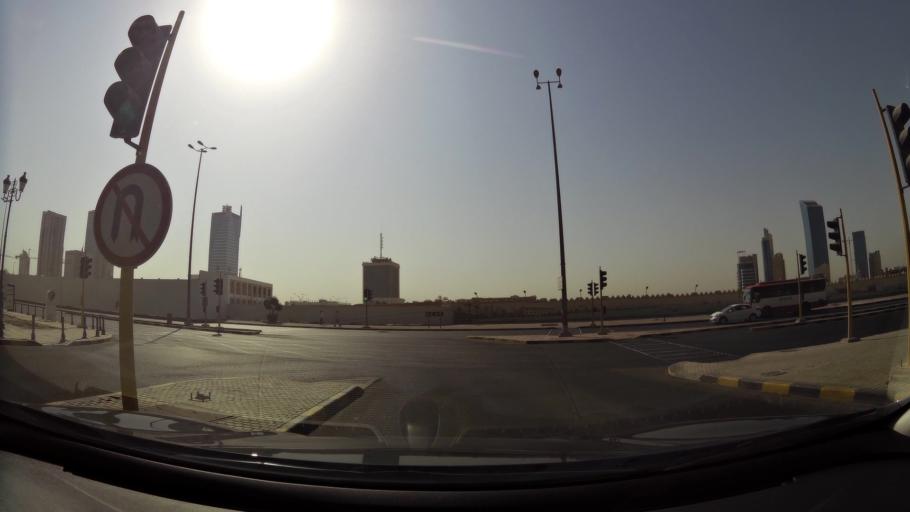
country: KW
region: Al Asimah
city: Kuwait City
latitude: 29.3663
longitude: 47.9708
